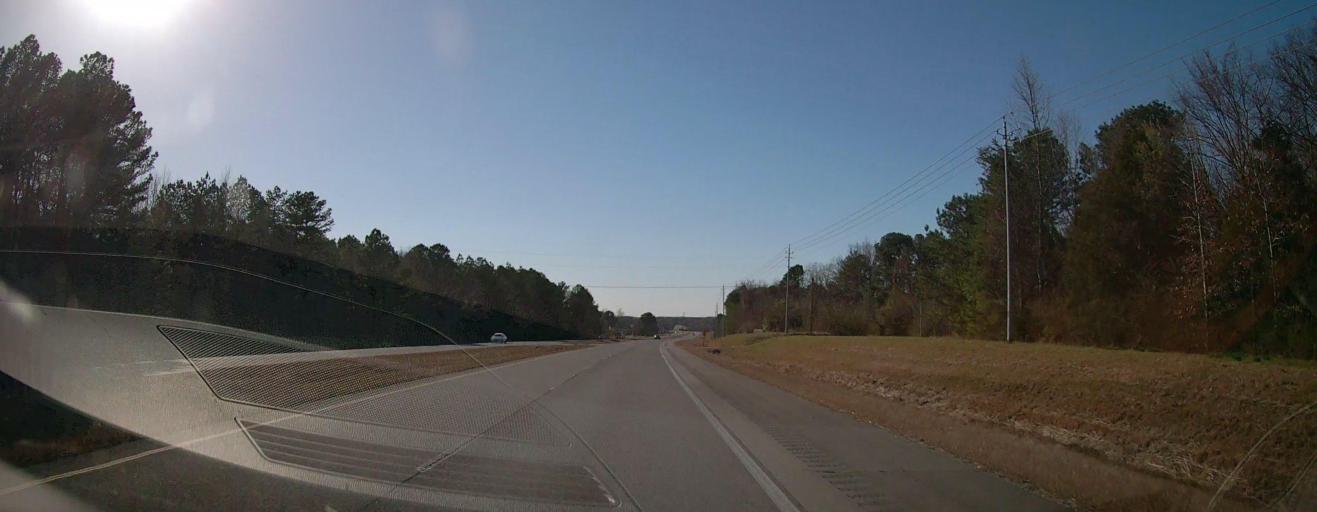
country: US
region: Alabama
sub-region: Colbert County
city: Cherokee
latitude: 34.7482
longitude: -87.9555
